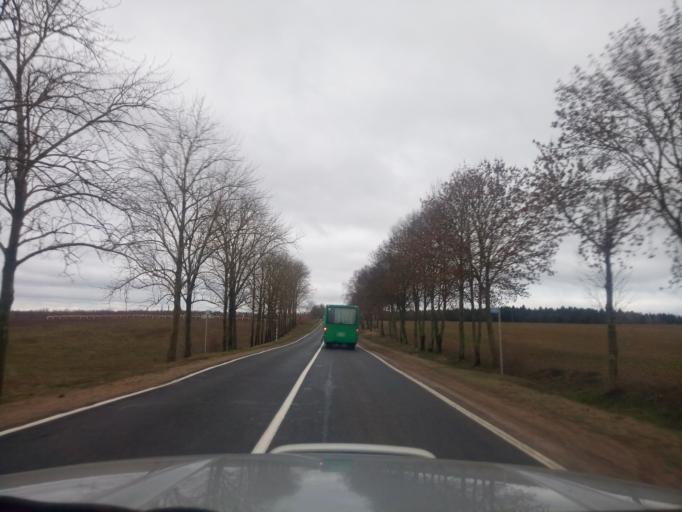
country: BY
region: Minsk
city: Kapyl'
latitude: 53.1718
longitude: 27.1571
